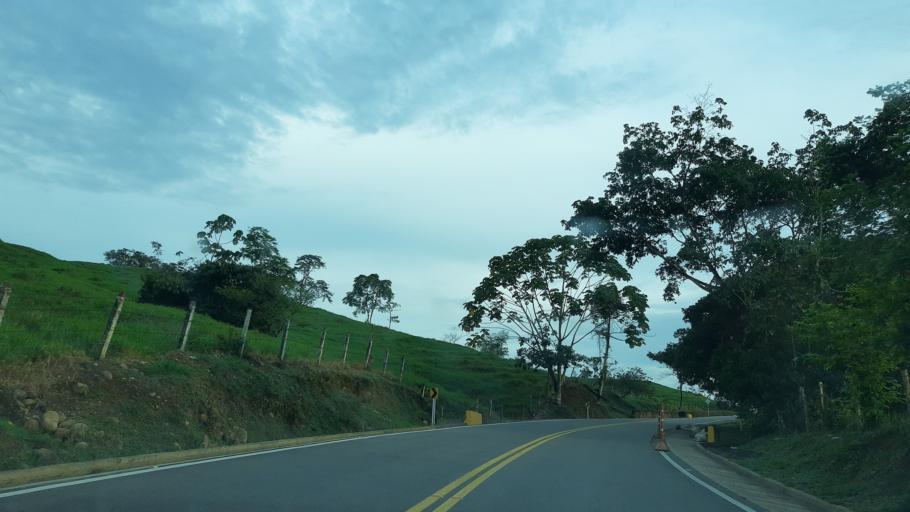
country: CO
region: Casanare
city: Sabanalarga
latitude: 4.7937
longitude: -73.0542
